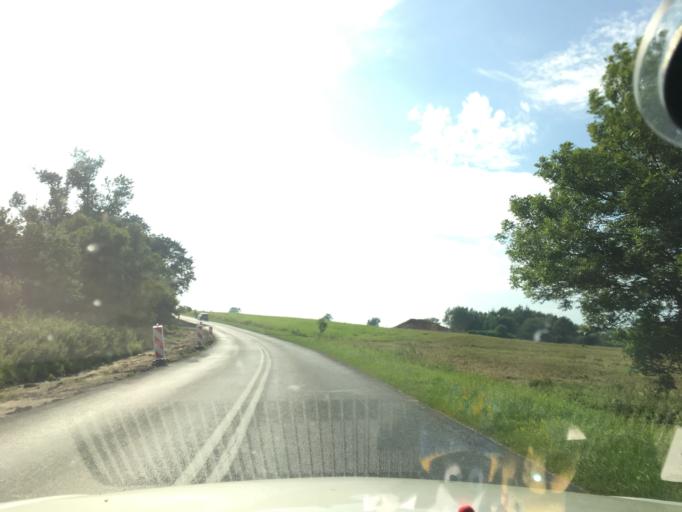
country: PL
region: West Pomeranian Voivodeship
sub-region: Powiat gryficki
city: Rewal
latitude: 54.0820
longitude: 15.0584
